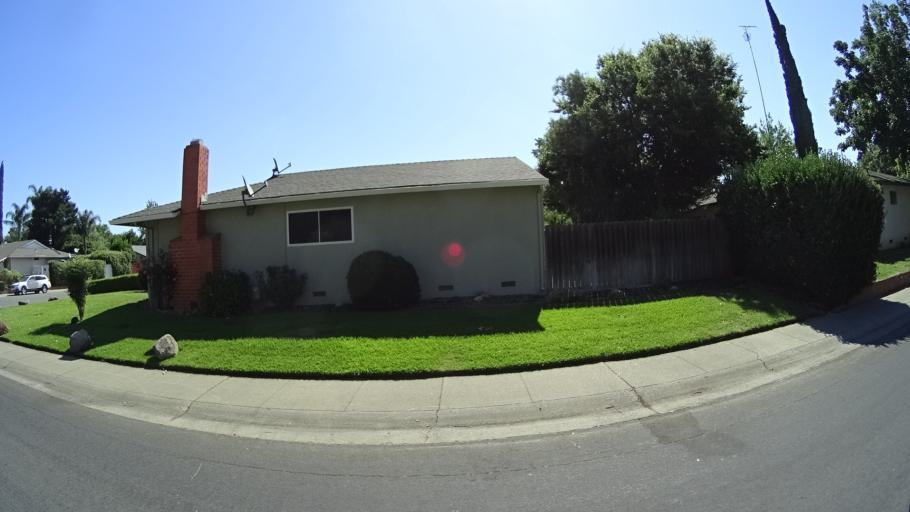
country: US
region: California
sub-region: Sacramento County
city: Rosemont
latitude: 38.5556
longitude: -121.3884
